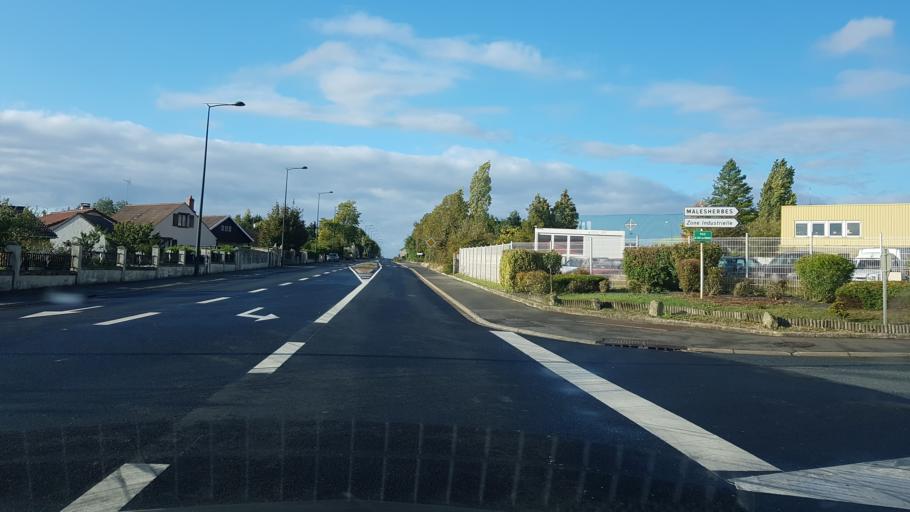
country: FR
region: Centre
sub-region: Departement du Loiret
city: Sermaises
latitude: 48.2900
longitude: 2.2040
